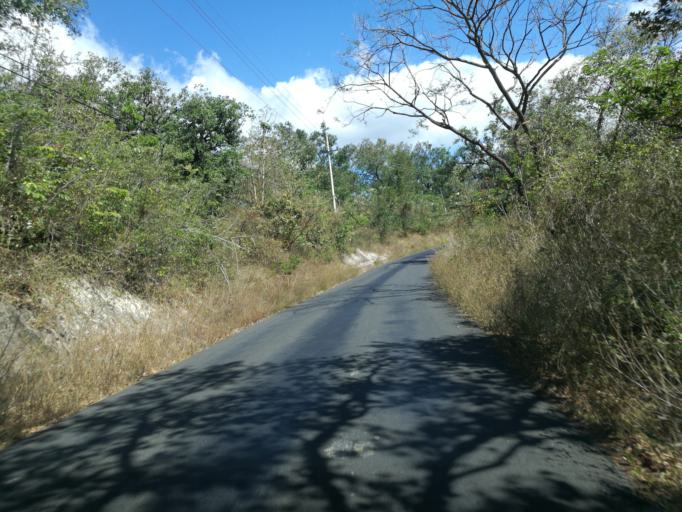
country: CR
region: Guanacaste
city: Liberia
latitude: 10.7402
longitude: -85.3867
